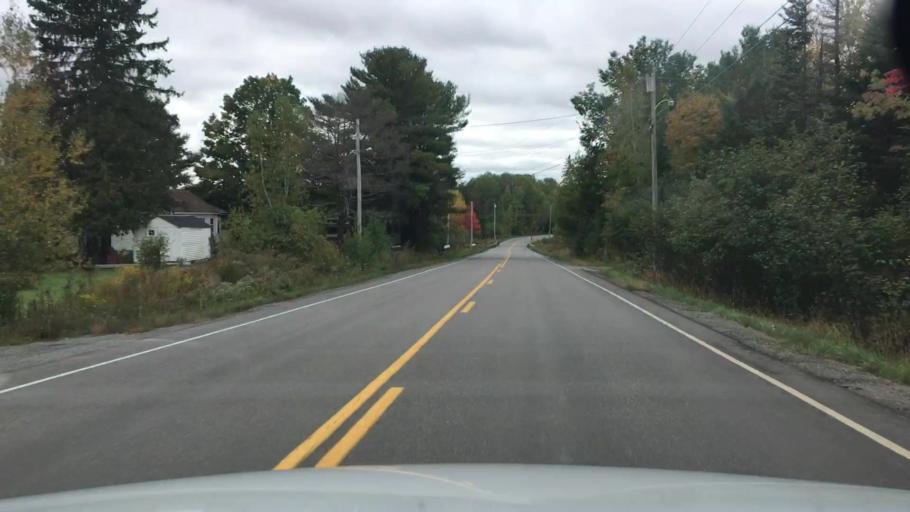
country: US
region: Maine
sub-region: Penobscot County
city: Hudson
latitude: 44.9873
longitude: -68.7697
